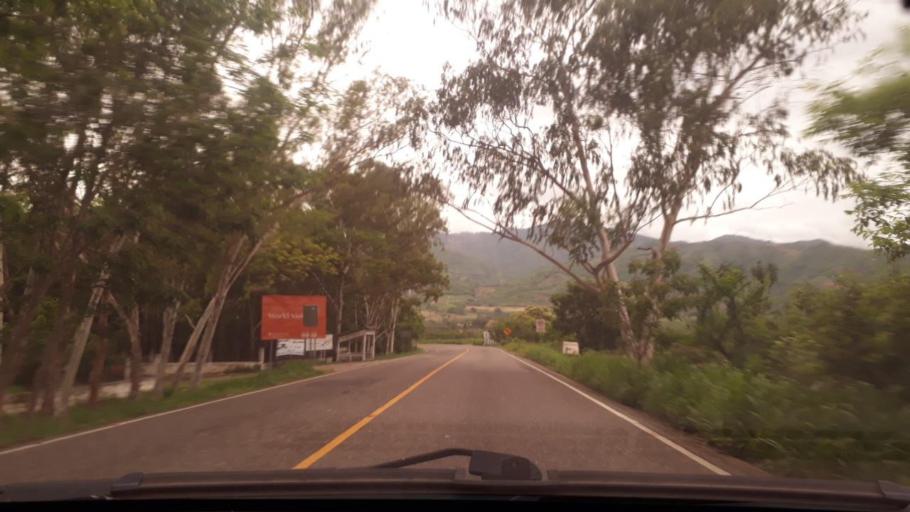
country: GT
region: Chiquimula
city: San Jose La Arada
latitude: 14.7405
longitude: -89.5536
